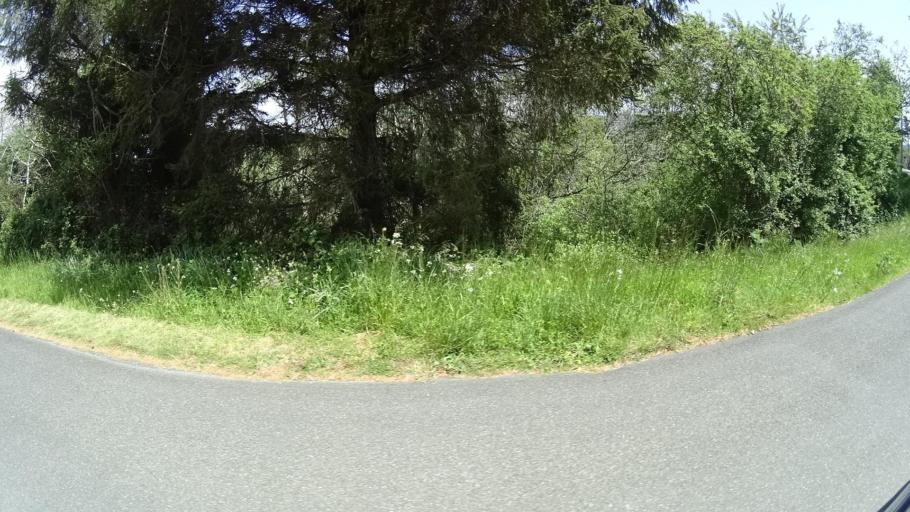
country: US
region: California
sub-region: Humboldt County
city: Humboldt Hill
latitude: 40.6751
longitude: -124.2224
